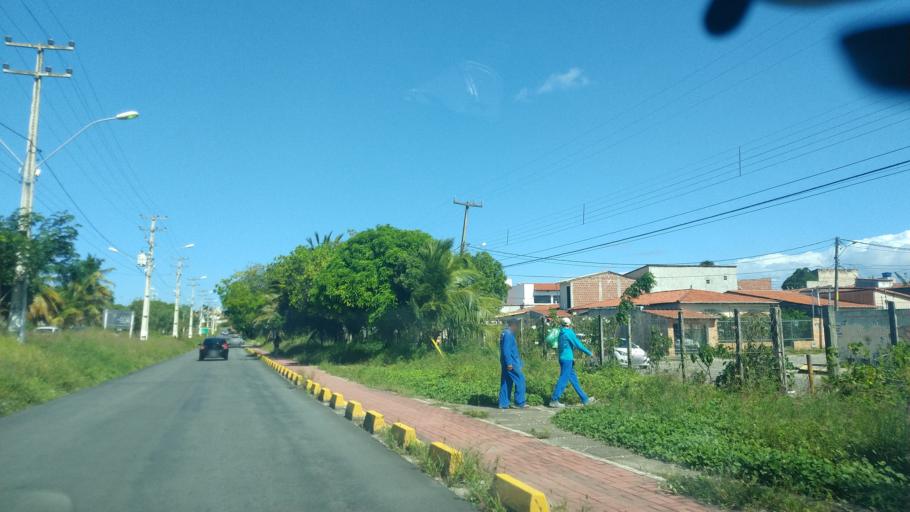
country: BR
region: Rio Grande do Norte
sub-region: Natal
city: Natal
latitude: -5.8401
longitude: -35.2044
